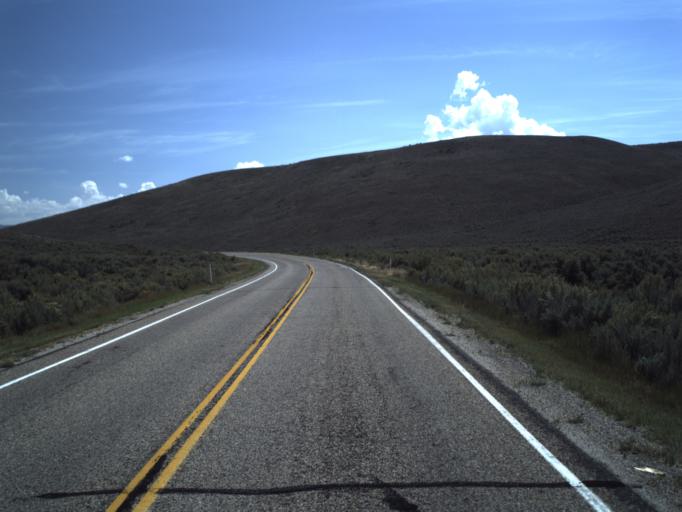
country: US
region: Utah
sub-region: Rich County
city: Randolph
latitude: 41.7710
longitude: -111.1748
